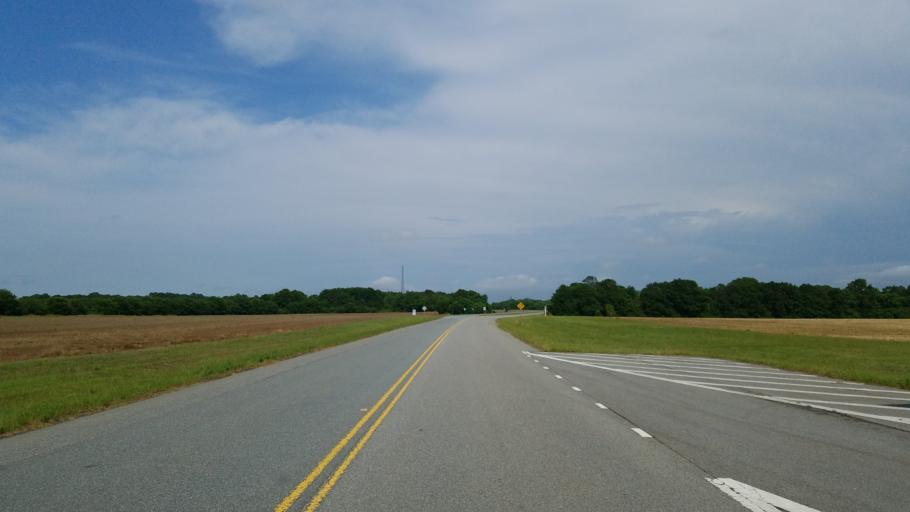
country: US
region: Georgia
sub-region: Houston County
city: Perry
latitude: 32.4360
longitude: -83.7744
